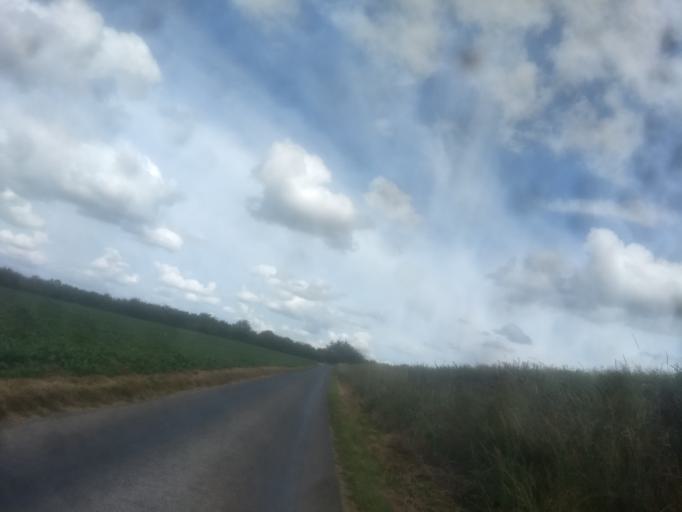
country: FR
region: Nord-Pas-de-Calais
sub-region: Departement du Pas-de-Calais
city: Duisans
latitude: 50.2909
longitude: 2.6963
